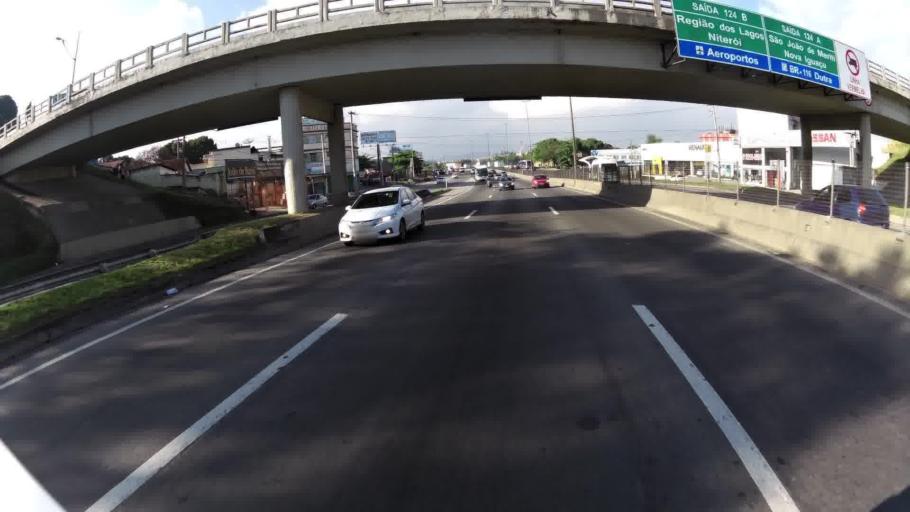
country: BR
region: Rio de Janeiro
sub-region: Duque De Caxias
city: Duque de Caxias
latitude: -22.8007
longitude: -43.2903
